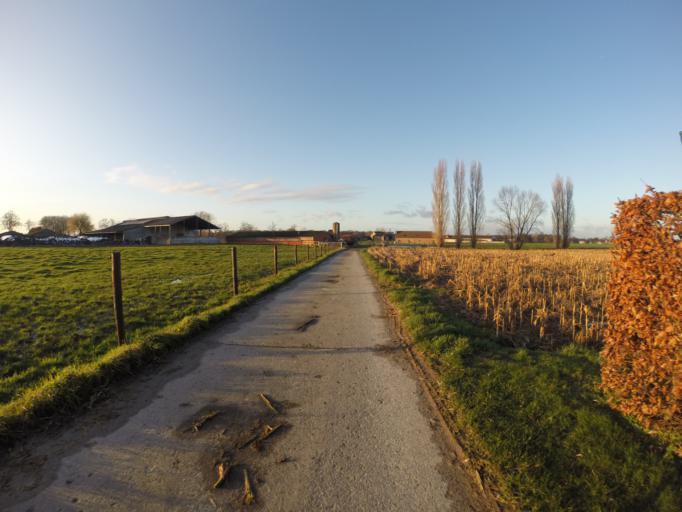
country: BE
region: Flanders
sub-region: Provincie Oost-Vlaanderen
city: Aalter
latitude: 51.0372
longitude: 3.4675
